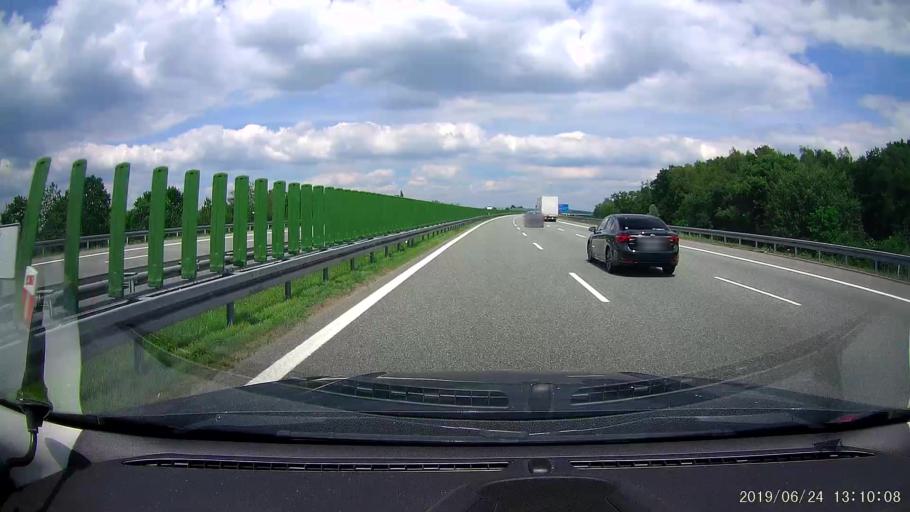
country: PL
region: Silesian Voivodeship
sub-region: Powiat gliwicki
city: Knurow
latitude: 50.2129
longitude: 18.6924
